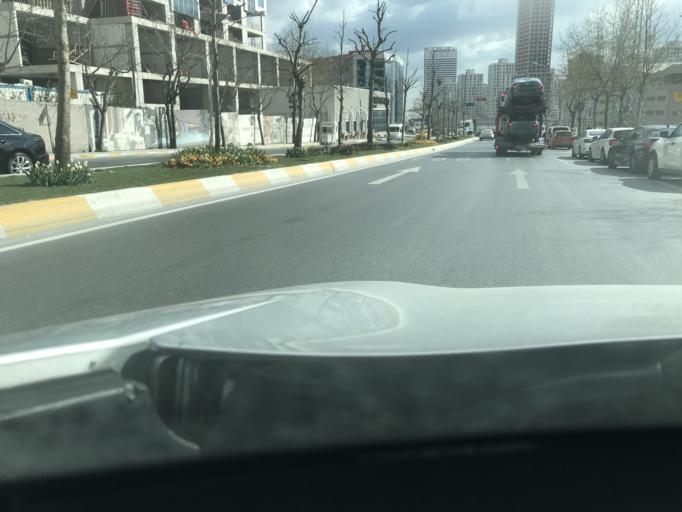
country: TR
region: Istanbul
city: Esenyurt
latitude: 41.0155
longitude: 28.6824
